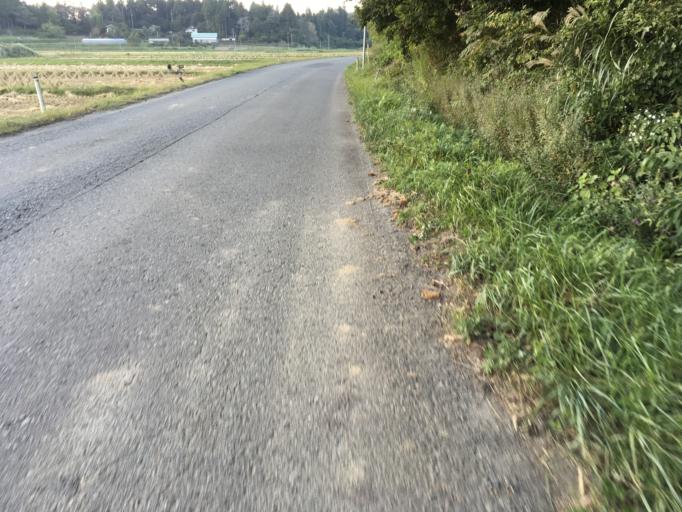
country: JP
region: Iwate
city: Ichinoseki
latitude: 38.7834
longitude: 141.2418
